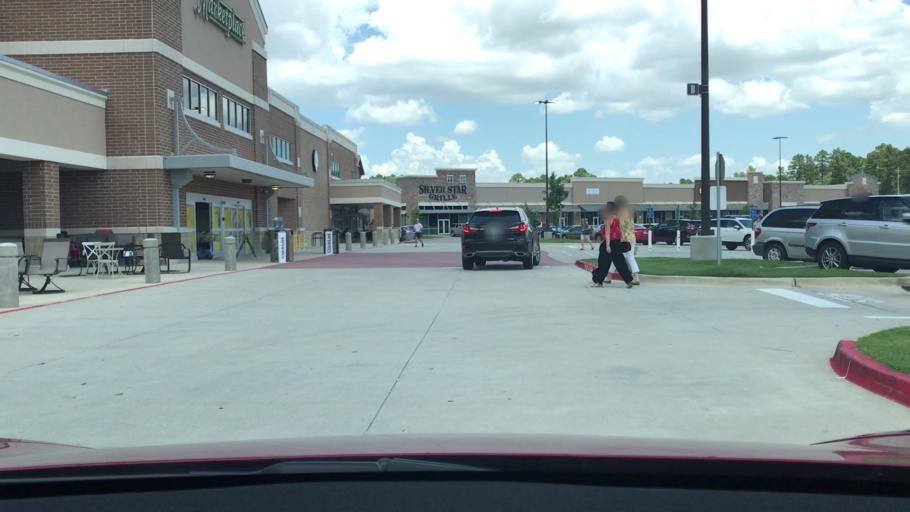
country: US
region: Louisiana
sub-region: Bossier Parish
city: Bossier City
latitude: 32.3939
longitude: -93.7285
